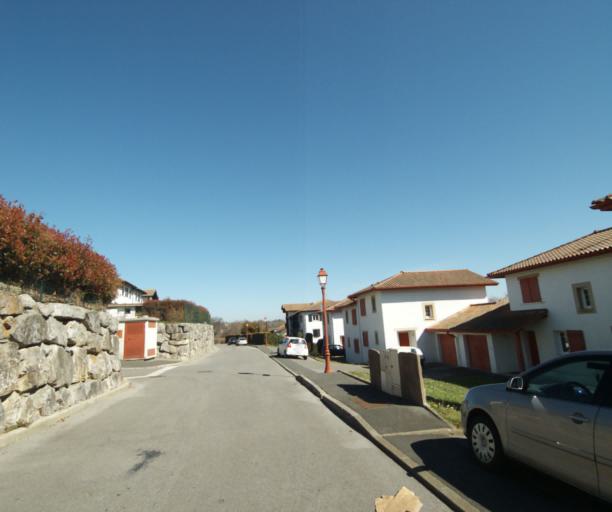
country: FR
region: Aquitaine
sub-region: Departement des Pyrenees-Atlantiques
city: Urrugne
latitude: 43.3458
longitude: -1.6934
